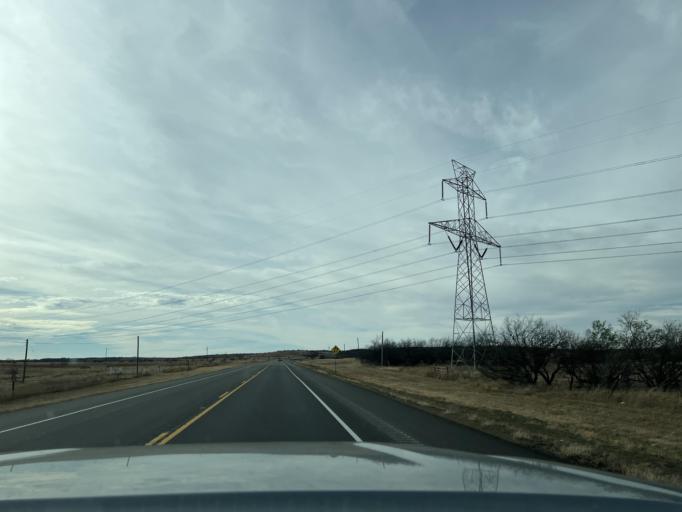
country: US
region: Texas
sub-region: Shackelford County
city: Albany
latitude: 32.7053
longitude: -99.4028
